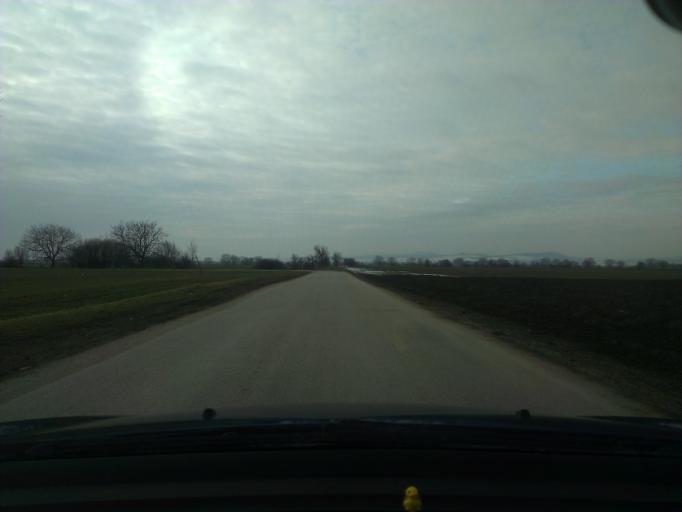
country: SK
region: Trnavsky
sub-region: Okres Trnava
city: Piestany
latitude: 48.6009
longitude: 17.8115
